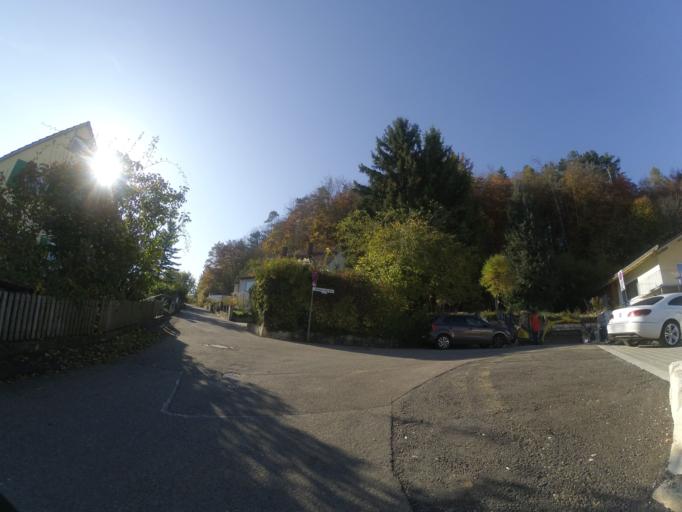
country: DE
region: Baden-Wuerttemberg
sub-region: Tuebingen Region
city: Blaubeuren
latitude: 48.4048
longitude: 9.7870
